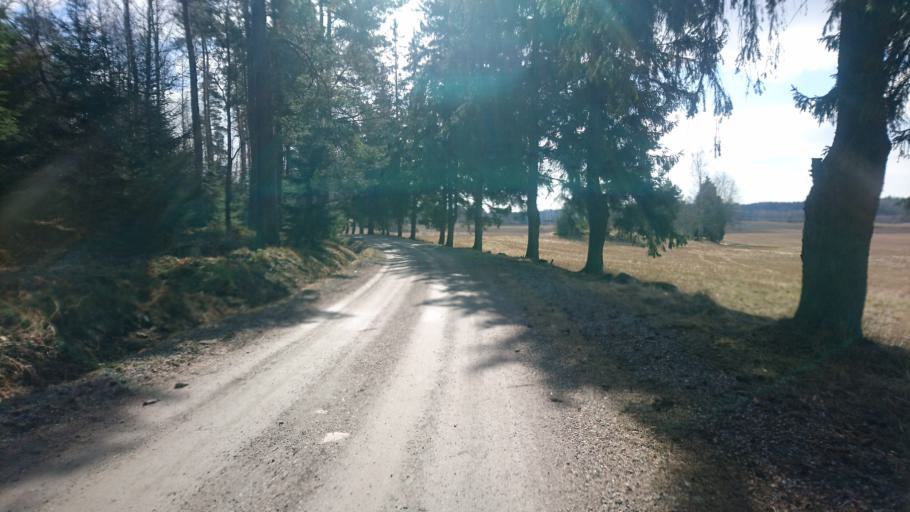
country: FI
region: Uusimaa
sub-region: Helsinki
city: Kauniainen
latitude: 60.1955
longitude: 24.7341
